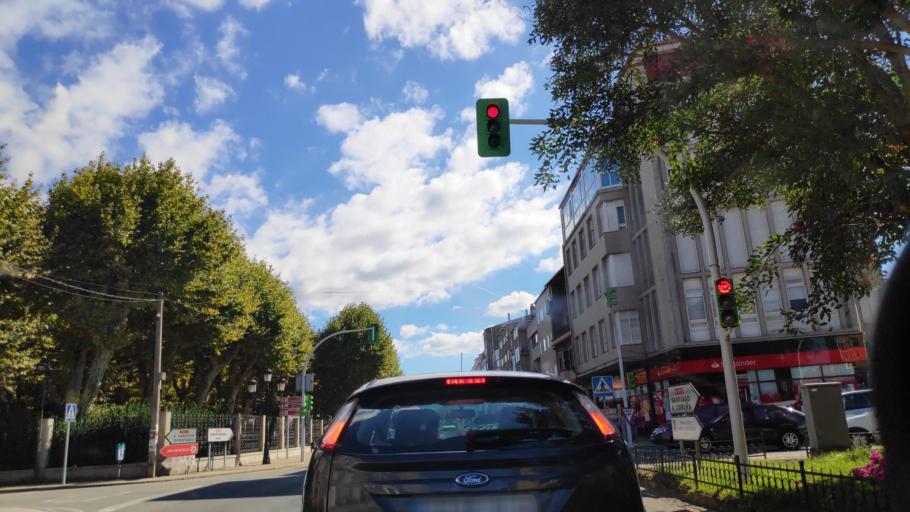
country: ES
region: Galicia
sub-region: Provincia da Coruna
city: Padron
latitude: 42.7394
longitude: -8.6590
